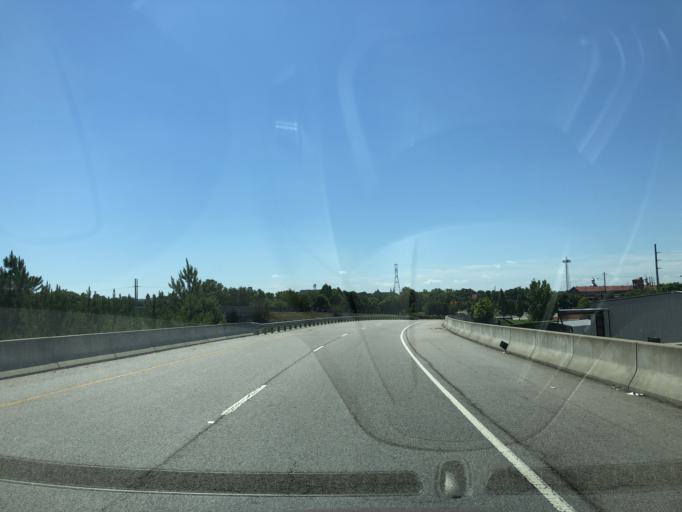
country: US
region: Georgia
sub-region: Richmond County
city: Augusta
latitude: 33.4834
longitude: -81.9859
